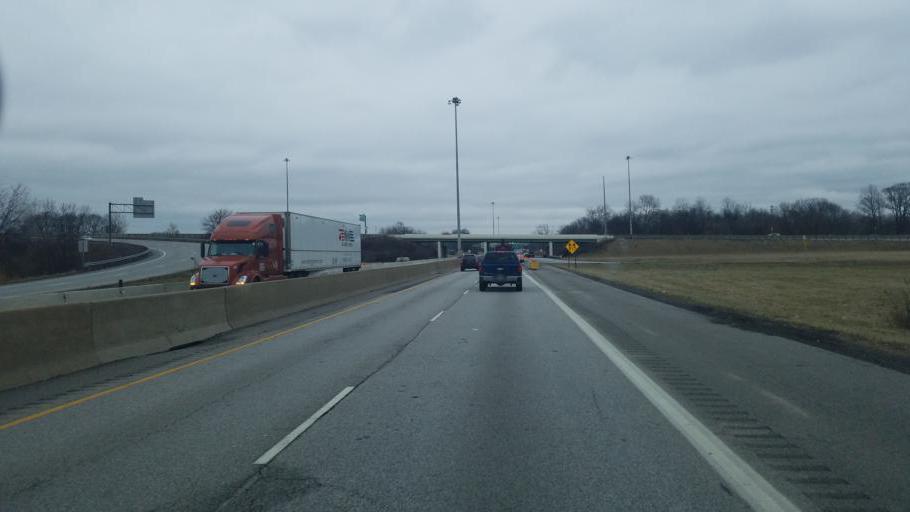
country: US
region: Ohio
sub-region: Summit County
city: Barberton
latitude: 41.0354
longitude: -81.5683
